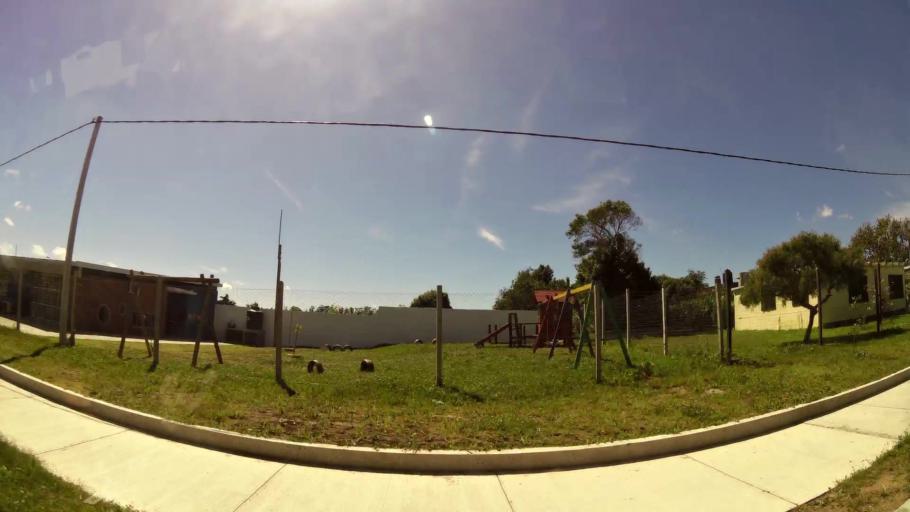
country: UY
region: Canelones
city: Paso de Carrasco
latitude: -34.8489
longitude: -56.1145
